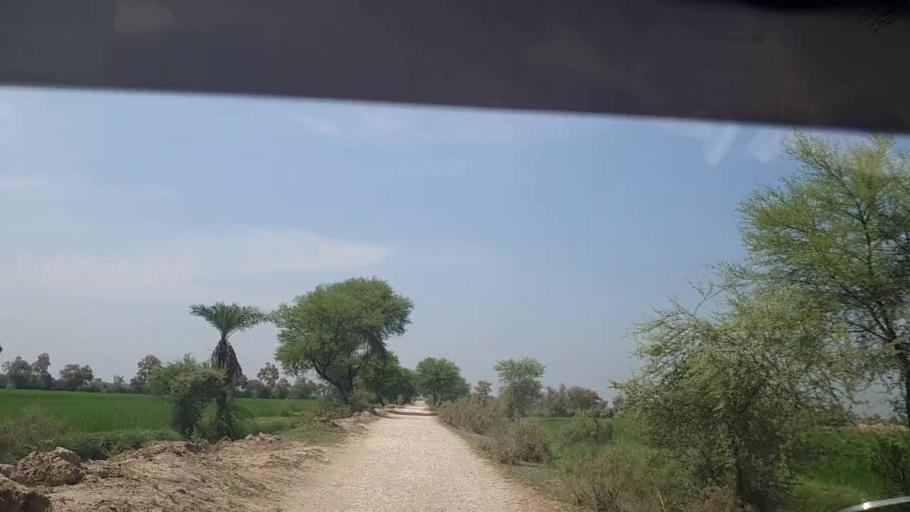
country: PK
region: Sindh
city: Thul
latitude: 28.2054
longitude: 68.6943
